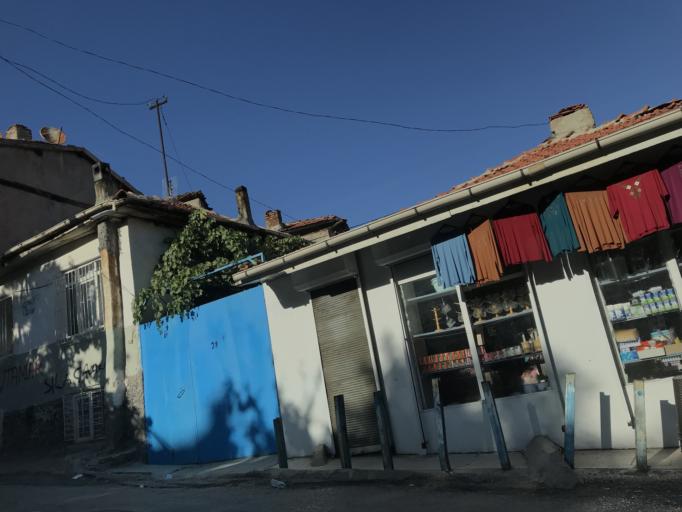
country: TR
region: Ankara
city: Cankaya
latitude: 39.9379
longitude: 32.8691
